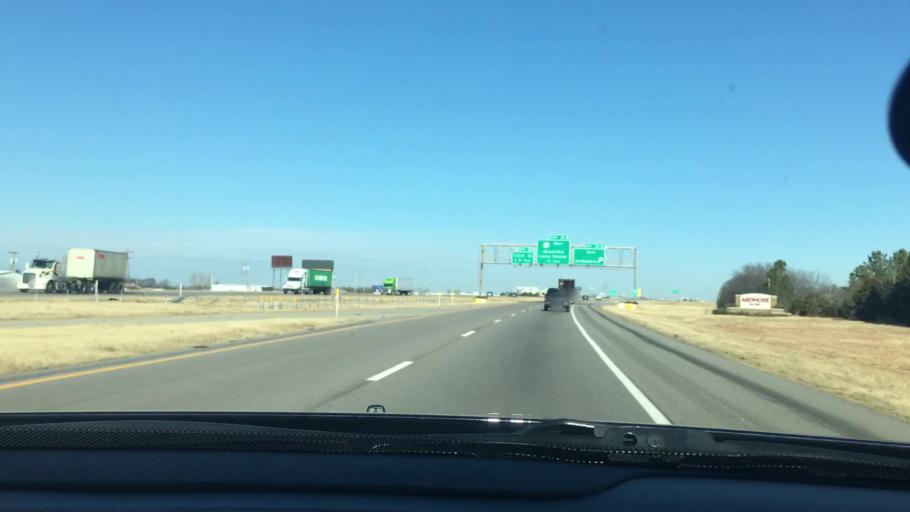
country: US
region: Oklahoma
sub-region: Carter County
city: Ardmore
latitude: 34.1665
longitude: -97.1670
